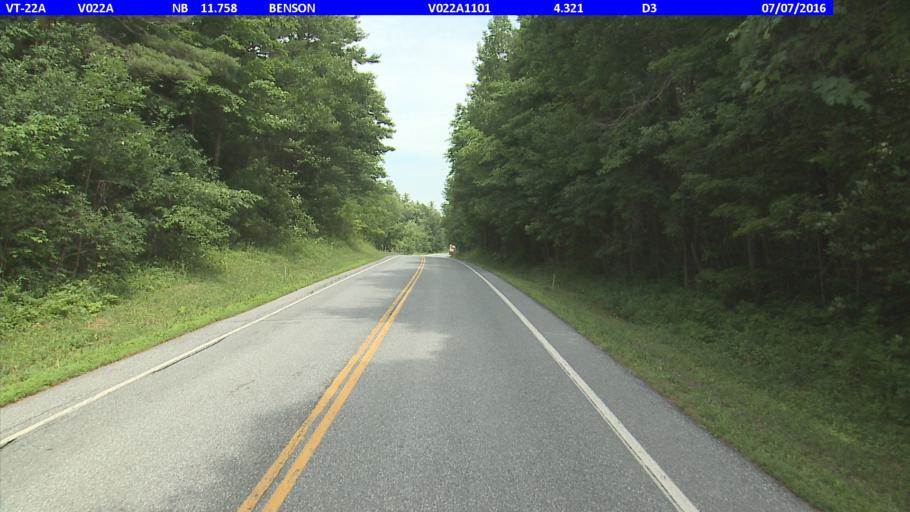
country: US
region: Vermont
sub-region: Rutland County
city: Fair Haven
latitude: 43.7301
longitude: -73.3031
